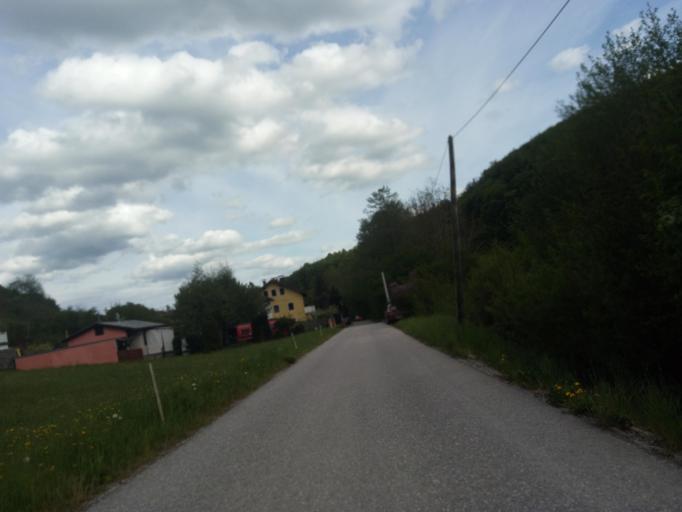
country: AT
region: Lower Austria
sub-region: Politischer Bezirk Wien-Umgebung
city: Wolfsgraben
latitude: 48.1274
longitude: 16.0856
